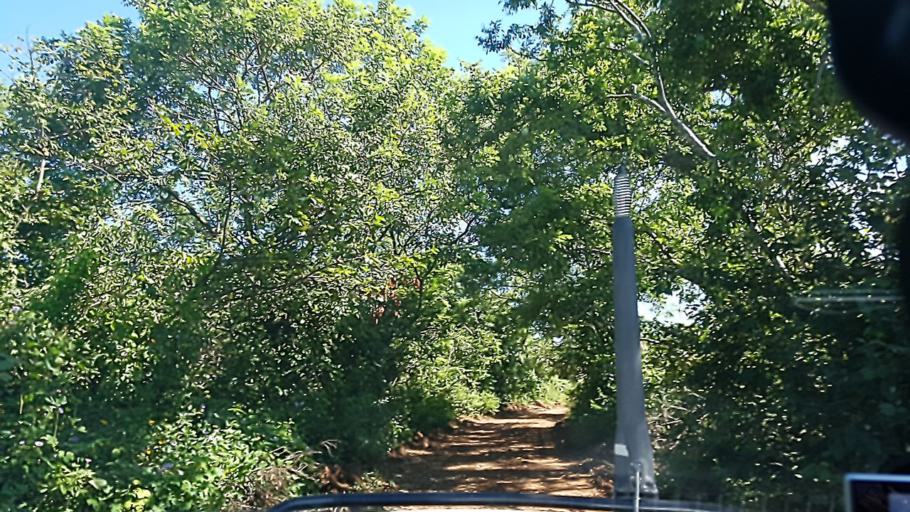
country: NI
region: Granada
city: Nandaime
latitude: 11.5679
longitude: -86.0906
